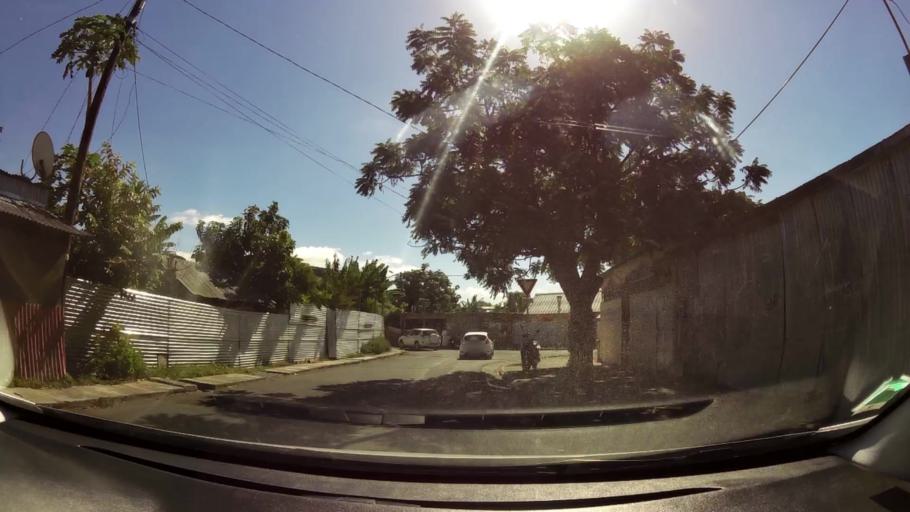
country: YT
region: Pamandzi
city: Pamandzi
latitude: -12.7865
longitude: 45.2767
